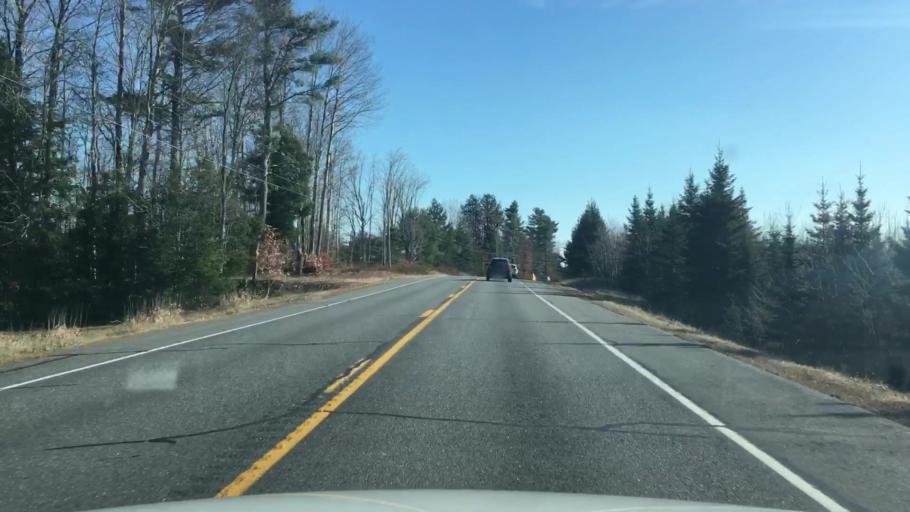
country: US
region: Maine
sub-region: Knox County
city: Washington
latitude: 44.2367
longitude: -69.3562
